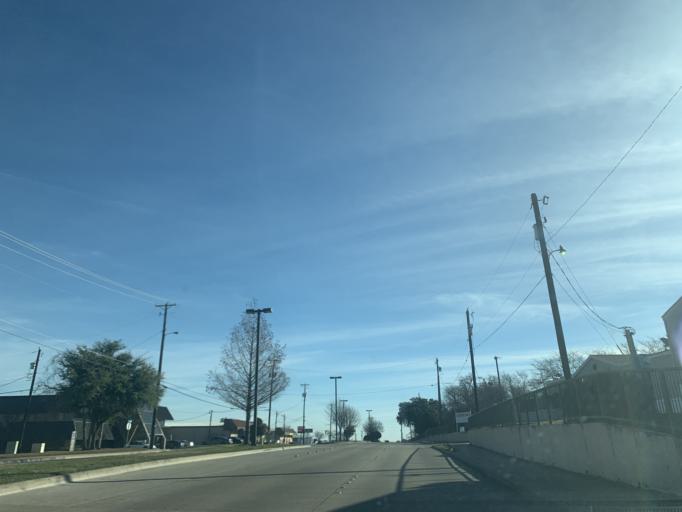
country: US
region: Texas
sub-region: Dallas County
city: DeSoto
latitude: 32.5751
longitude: -96.8279
